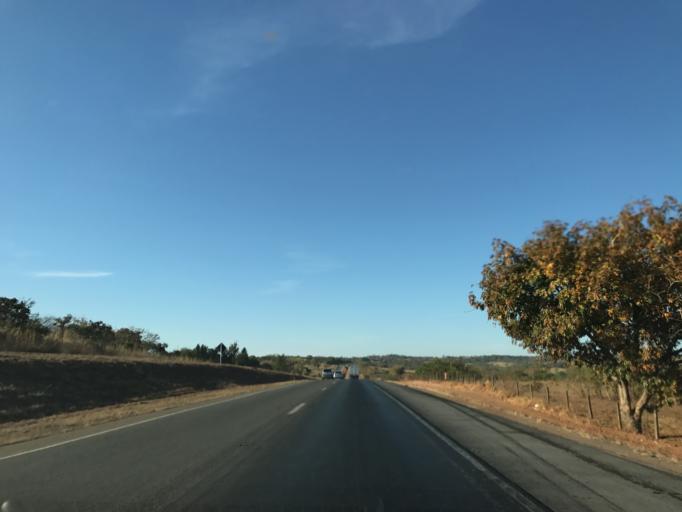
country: BR
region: Goias
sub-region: Hidrolandia
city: Hidrolandia
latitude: -16.8959
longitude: -49.2556
